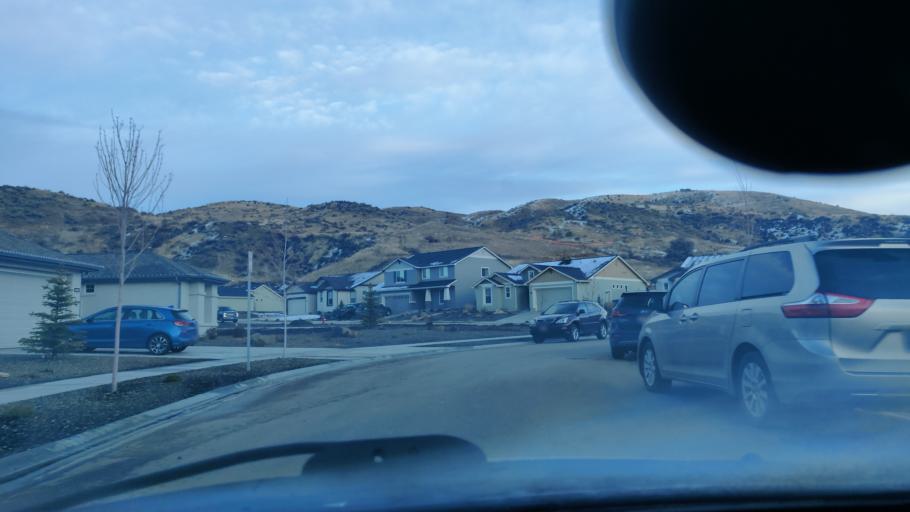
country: US
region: Idaho
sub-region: Ada County
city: Eagle
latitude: 43.7880
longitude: -116.2612
